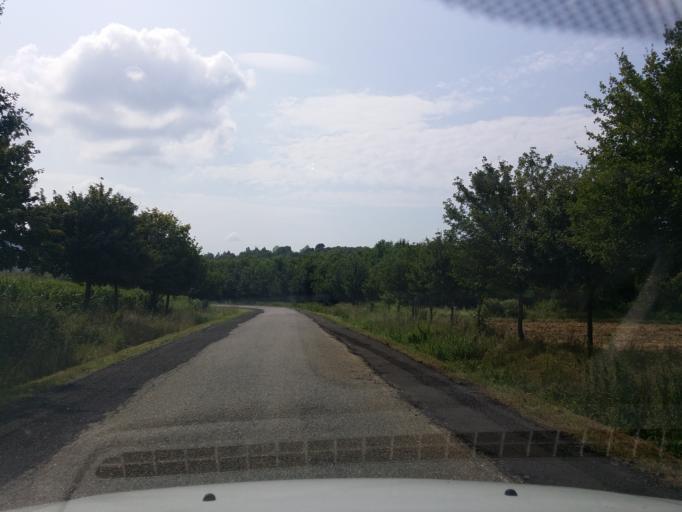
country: HU
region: Borsod-Abauj-Zemplen
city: Sarospatak
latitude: 48.4664
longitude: 21.5234
